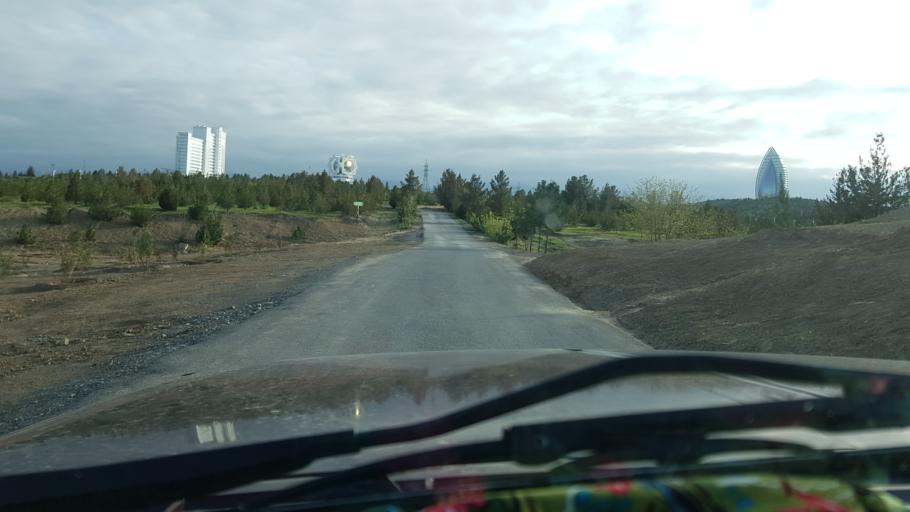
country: TM
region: Ahal
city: Ashgabat
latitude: 37.9379
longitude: 58.3466
